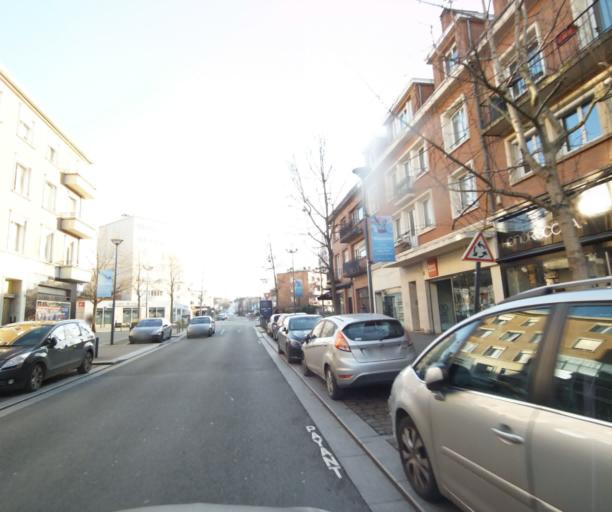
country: FR
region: Nord-Pas-de-Calais
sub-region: Departement du Nord
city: Valenciennes
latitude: 50.3584
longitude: 3.5263
